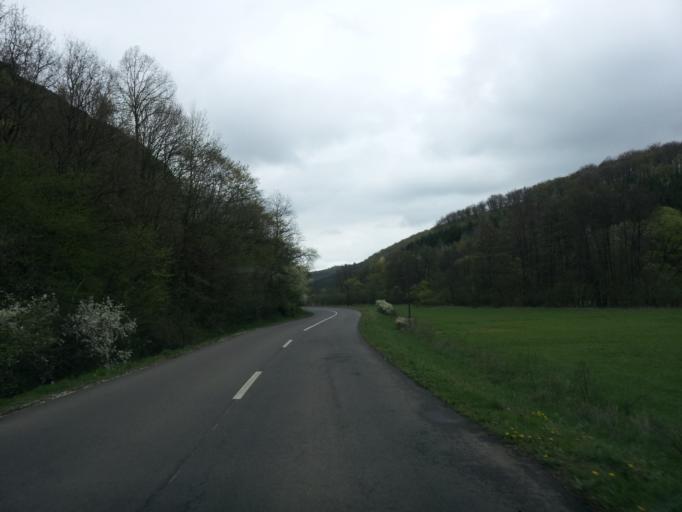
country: HU
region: Borsod-Abauj-Zemplen
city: Rudabanya
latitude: 48.4786
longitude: 20.5783
